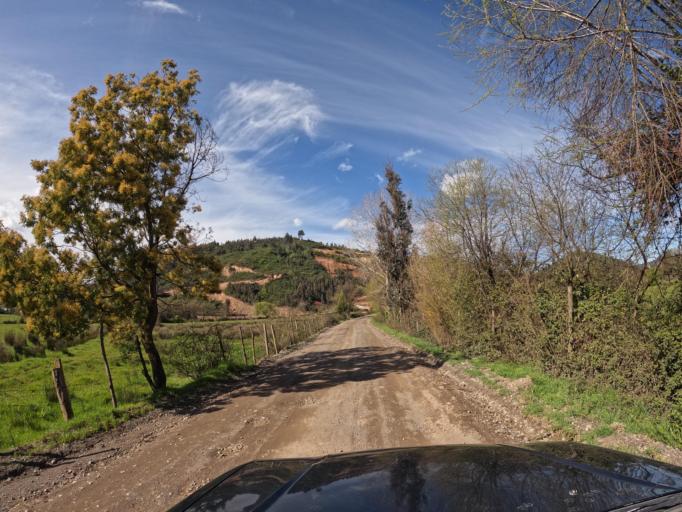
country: CL
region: Biobio
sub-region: Provincia de Concepcion
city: Chiguayante
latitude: -37.0636
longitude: -72.8869
